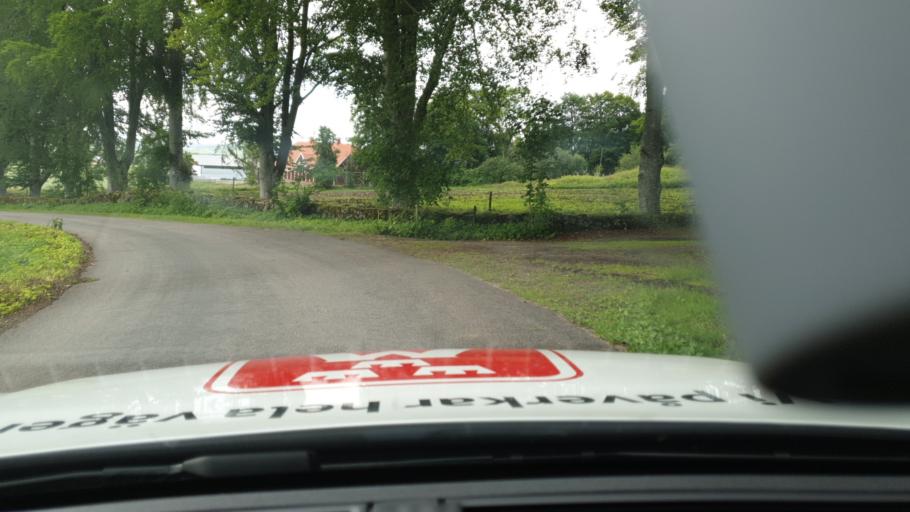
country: SE
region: Vaestra Goetaland
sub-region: Falkopings Kommun
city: Falkoeping
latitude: 58.1302
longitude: 13.6119
